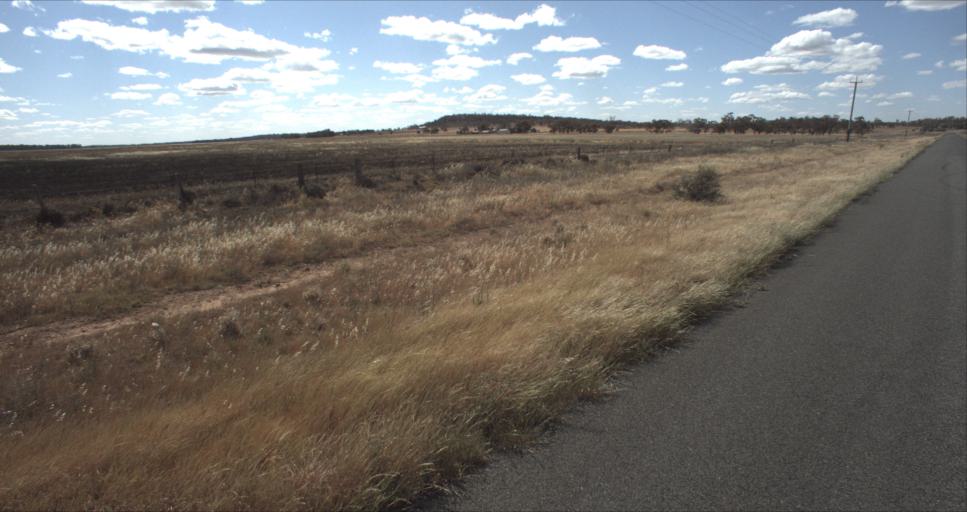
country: AU
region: New South Wales
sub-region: Leeton
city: Leeton
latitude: -34.4333
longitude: 146.2578
